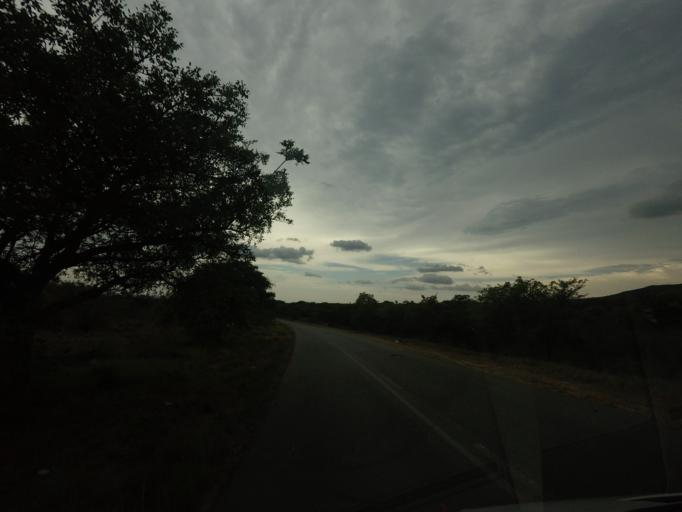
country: ZA
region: Limpopo
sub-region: Mopani District Municipality
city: Hoedspruit
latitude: -24.5077
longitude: 30.9103
